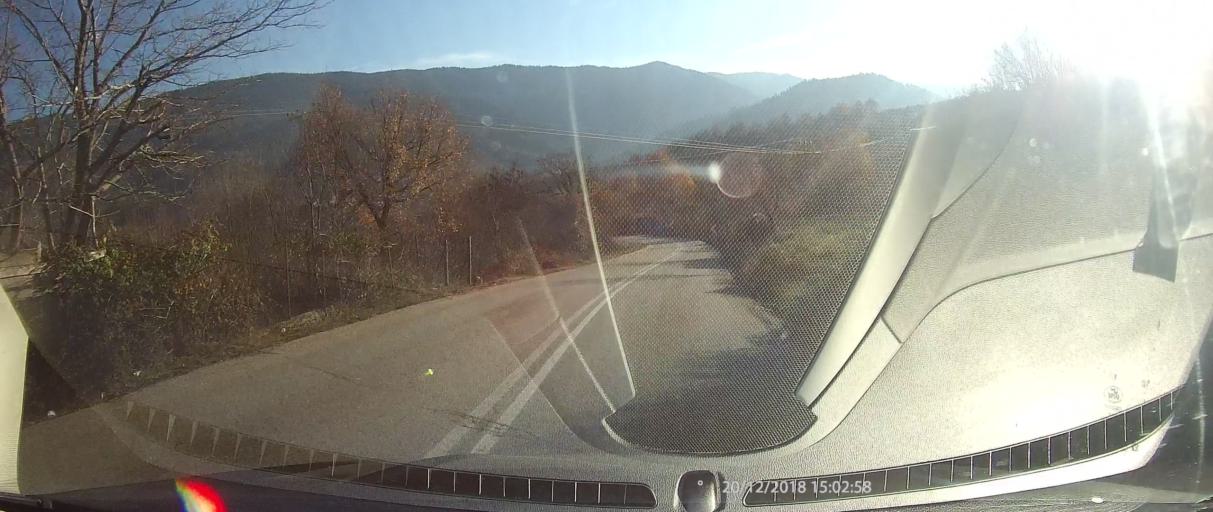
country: GR
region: Central Greece
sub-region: Nomos Evrytanias
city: Karpenisi
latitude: 38.9119
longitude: 21.9215
